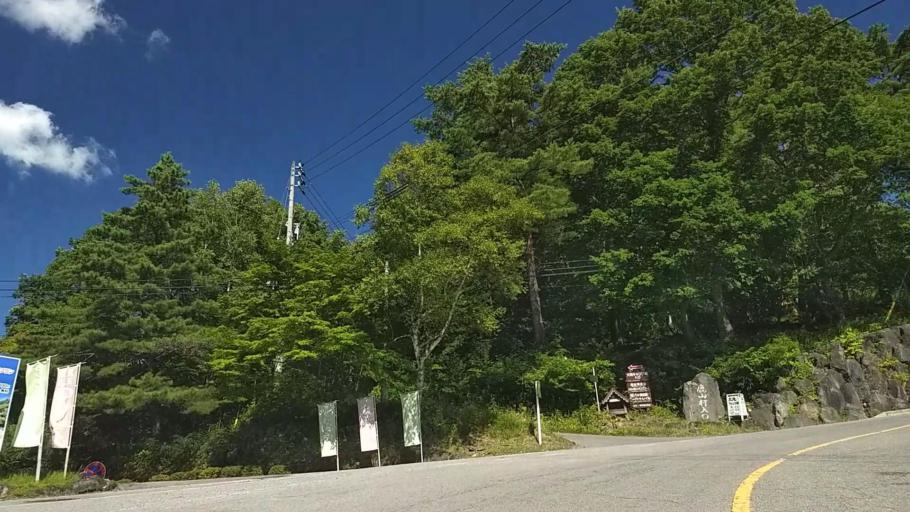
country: JP
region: Nagano
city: Chino
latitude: 36.0574
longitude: 138.2628
